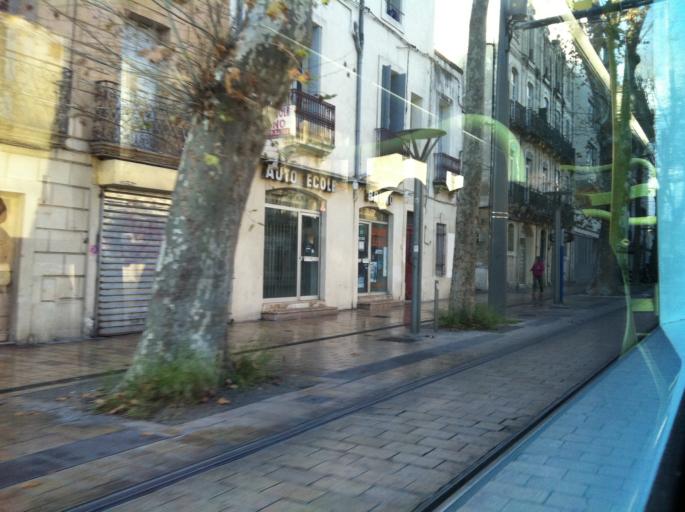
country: FR
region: Languedoc-Roussillon
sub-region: Departement de l'Herault
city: Montpellier
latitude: 43.6151
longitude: 3.8756
